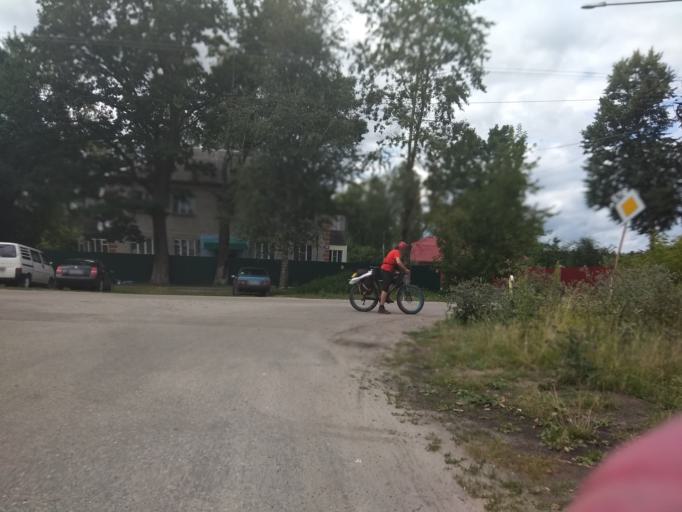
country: RU
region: Moskovskaya
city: Misheronskiy
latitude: 55.7203
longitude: 39.7411
